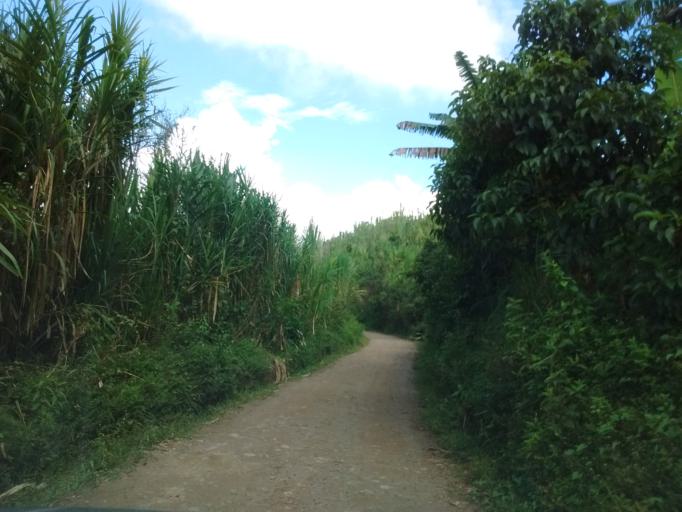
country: CO
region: Cauca
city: Morales
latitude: 2.6879
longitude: -76.7368
